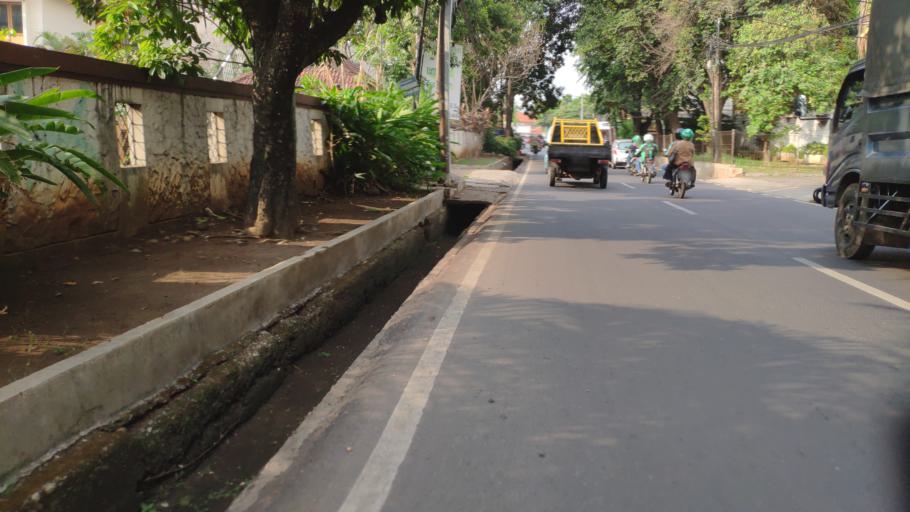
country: ID
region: West Java
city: Pamulang
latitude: -6.3147
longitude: 106.8125
